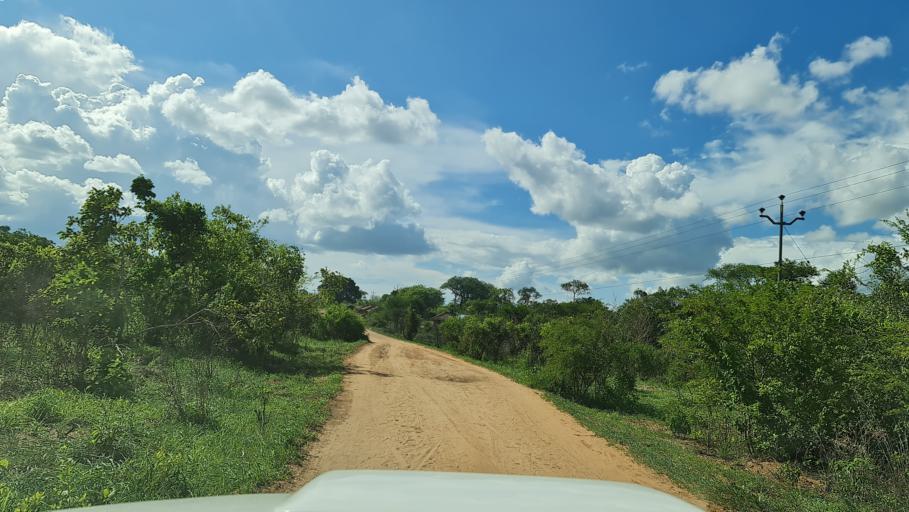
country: MZ
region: Nampula
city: Ilha de Mocambique
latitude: -15.4374
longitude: 40.2820
